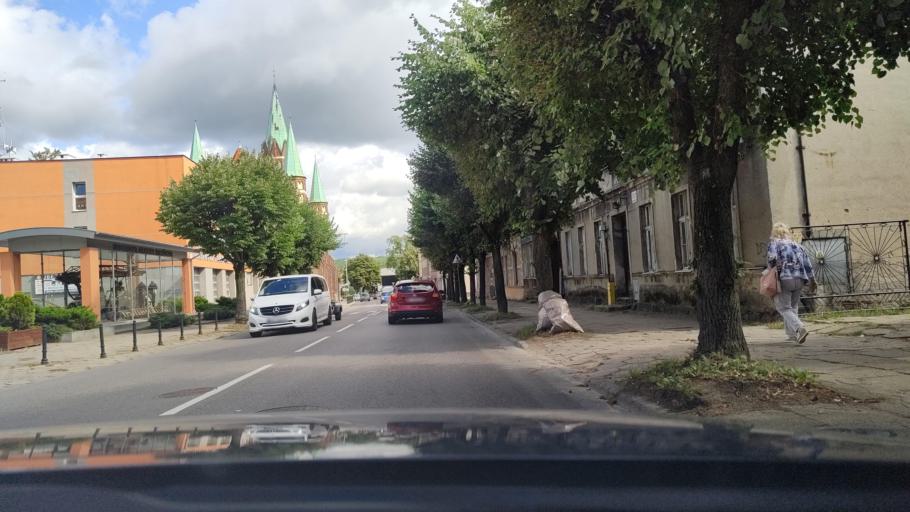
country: PL
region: Pomeranian Voivodeship
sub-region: Powiat wejherowski
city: Wejherowo
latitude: 54.6011
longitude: 18.2334
